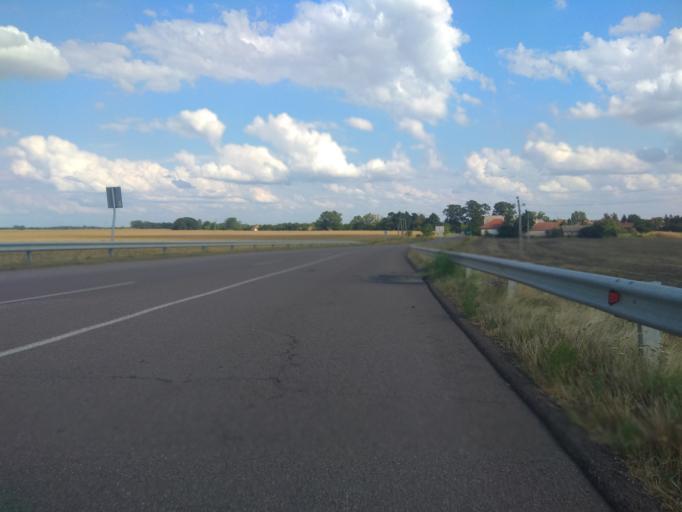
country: HU
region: Borsod-Abauj-Zemplen
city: Mezokeresztes
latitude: 47.8123
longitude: 20.7165
